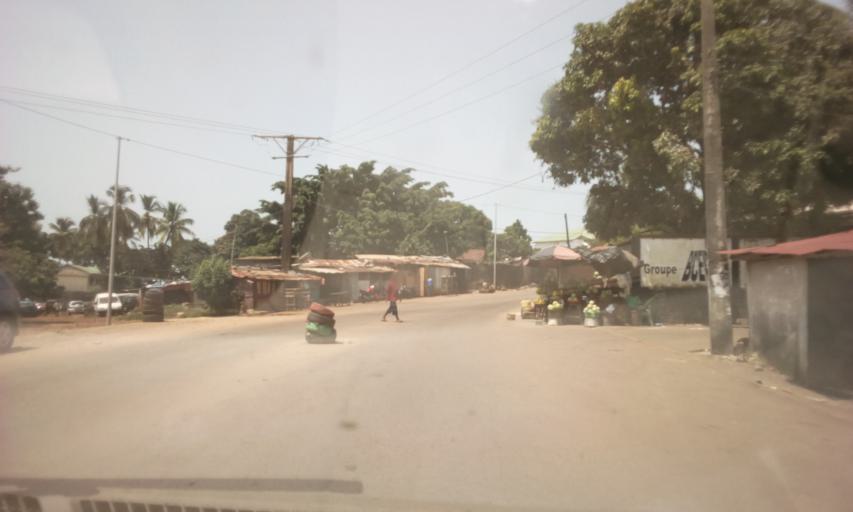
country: GN
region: Conakry
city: Conakry
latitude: 9.5734
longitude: -13.6645
